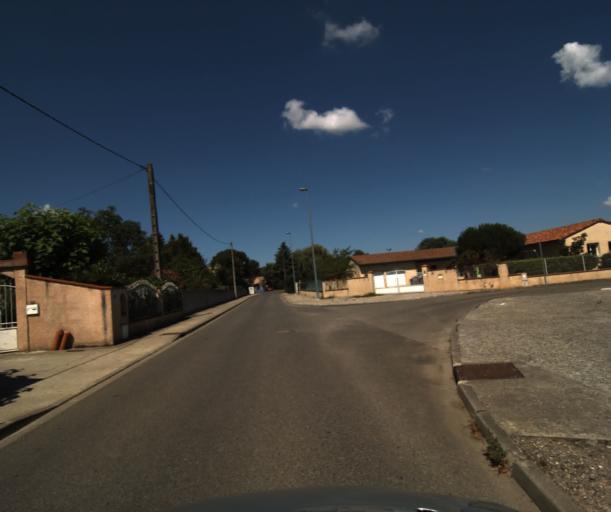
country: FR
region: Midi-Pyrenees
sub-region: Departement de la Haute-Garonne
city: Eaunes
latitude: 43.4269
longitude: 1.3492
